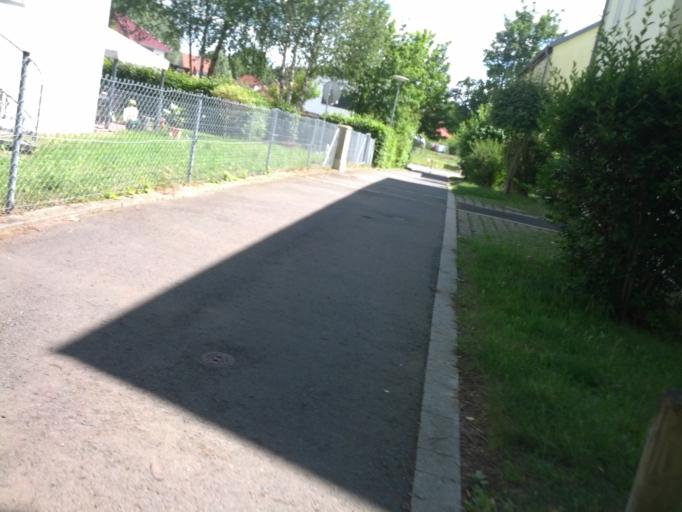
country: DE
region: Thuringia
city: Bischofroda
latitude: 51.0084
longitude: 10.3581
